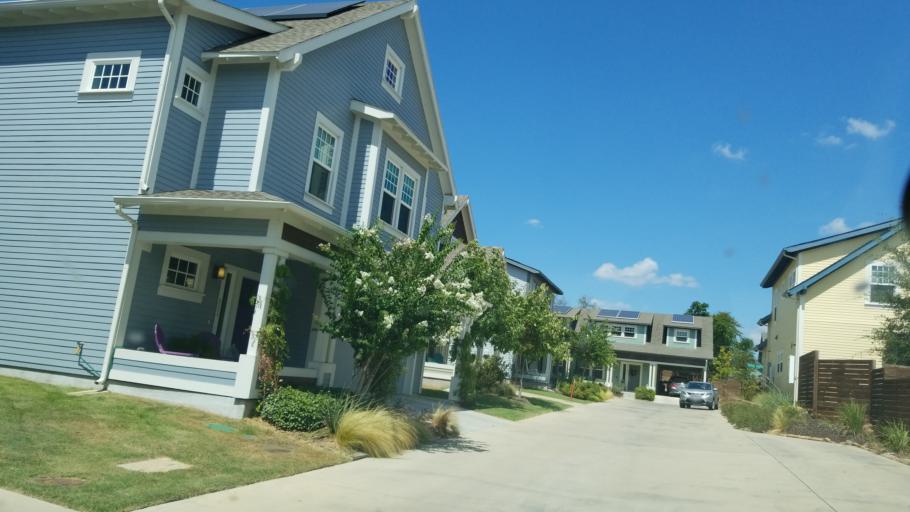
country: US
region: Texas
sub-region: Dallas County
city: Dallas
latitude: 32.7534
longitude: -96.8326
